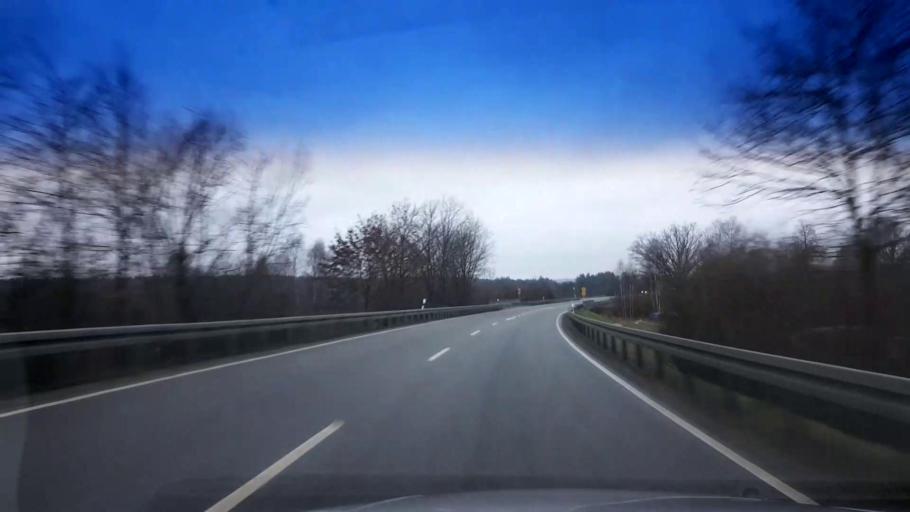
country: DE
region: Bavaria
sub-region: Upper Palatinate
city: Tirschenreuth
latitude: 49.8643
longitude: 12.2575
